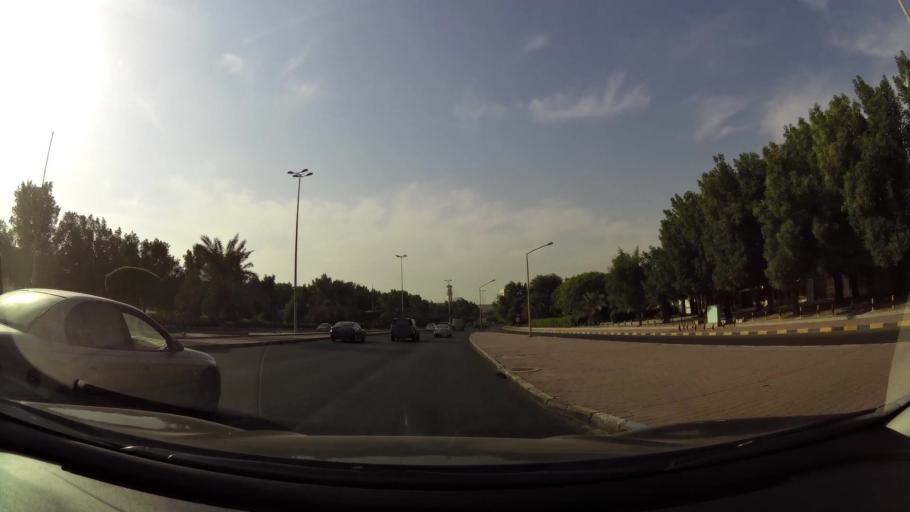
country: KW
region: Muhafazat Hawalli
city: Salwa
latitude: 29.2735
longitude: 48.0887
